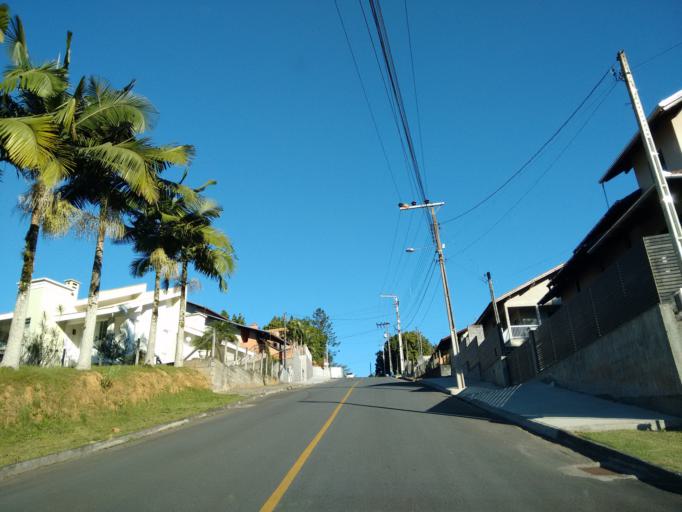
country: BR
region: Santa Catarina
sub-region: Pomerode
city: Pomerode
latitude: -26.7523
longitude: -49.1671
